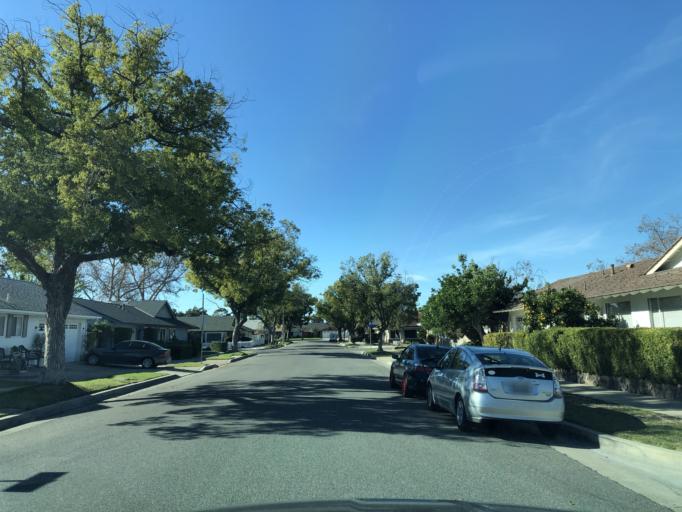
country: US
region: California
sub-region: Orange County
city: Orange
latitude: 33.7753
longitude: -117.8280
